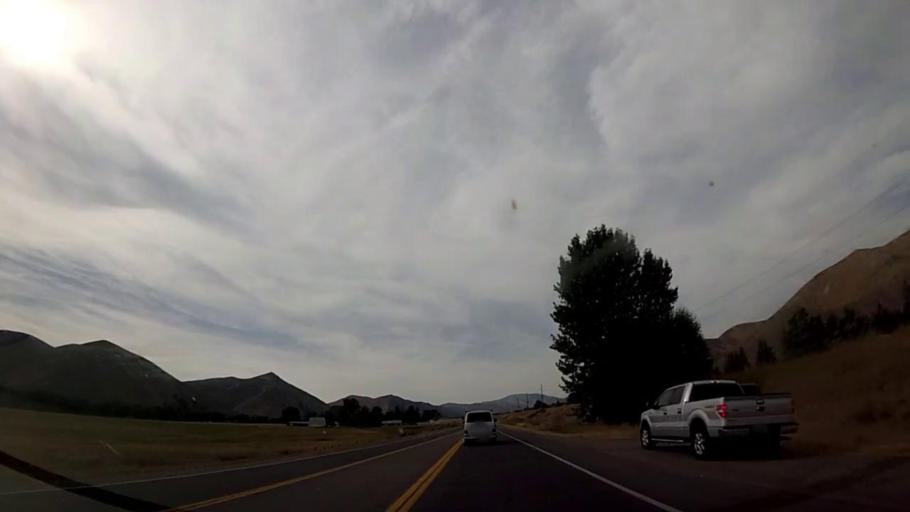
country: US
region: Idaho
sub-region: Blaine County
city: Bellevue
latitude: 43.4878
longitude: -114.2783
